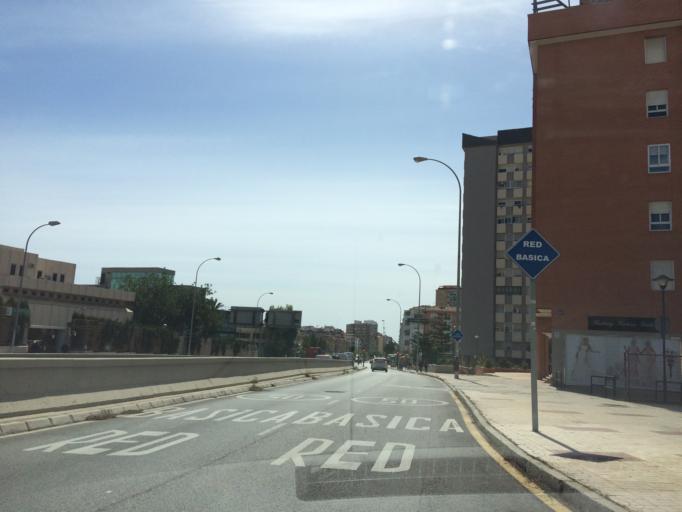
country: ES
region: Andalusia
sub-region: Provincia de Malaga
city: Malaga
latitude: 36.7137
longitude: -4.4477
